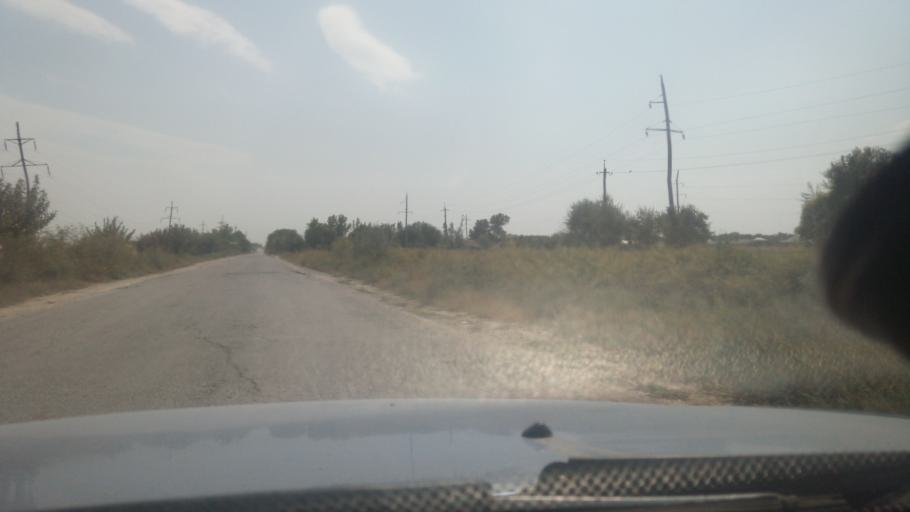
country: UZ
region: Sirdaryo
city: Guliston
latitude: 40.5313
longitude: 68.7667
